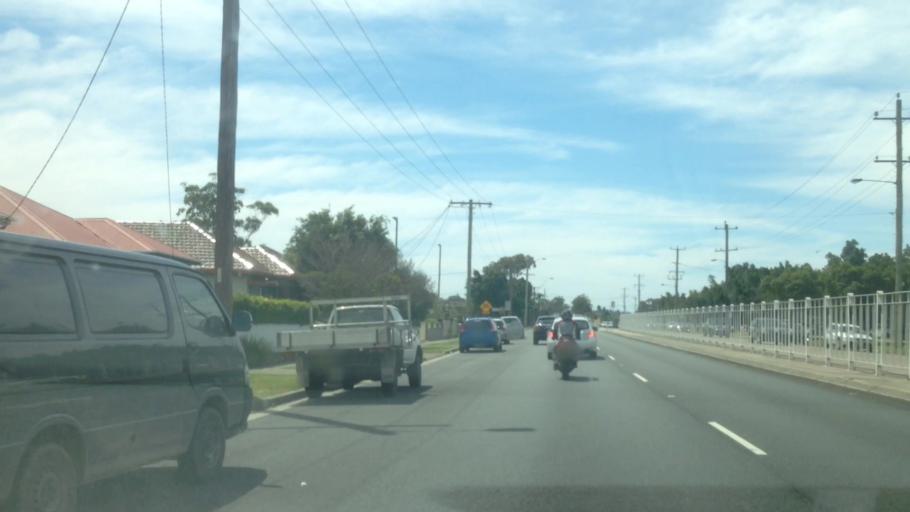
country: AU
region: New South Wales
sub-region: Newcastle
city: Broadmeadow
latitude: -32.9213
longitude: 151.7235
